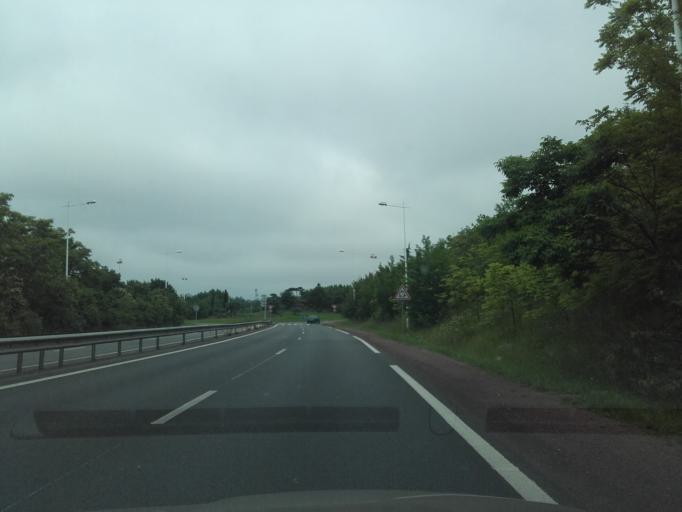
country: FR
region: Centre
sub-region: Departement d'Indre-et-Loire
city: Rochecorbon
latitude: 47.4187
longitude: 0.7178
